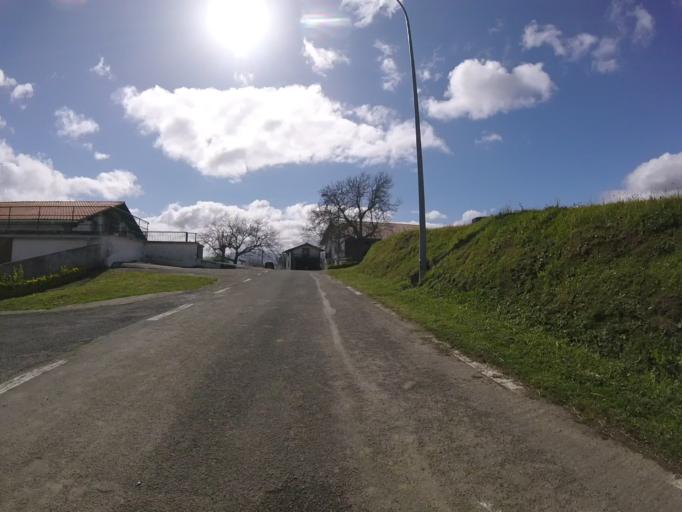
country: ES
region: Basque Country
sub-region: Provincia de Guipuzcoa
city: Albiztur
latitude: 43.1339
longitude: -2.1078
